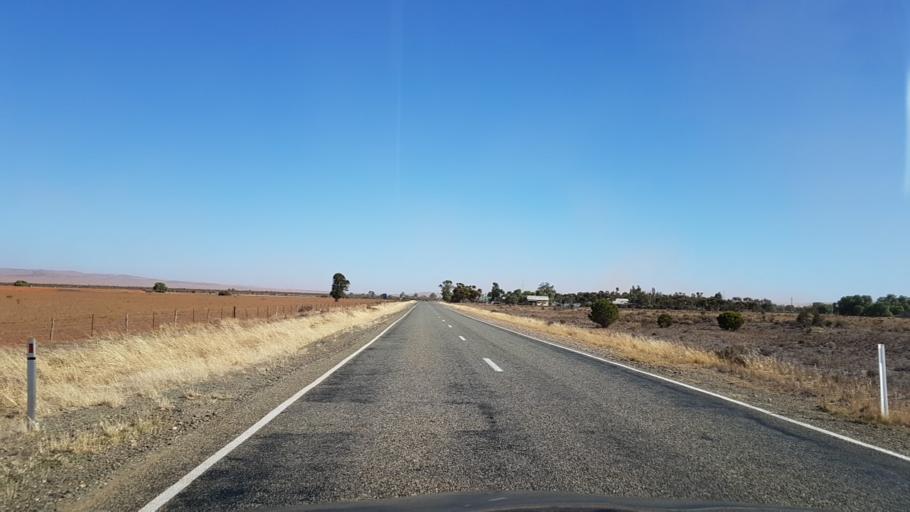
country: AU
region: South Australia
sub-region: Peterborough
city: Peterborough
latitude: -33.1489
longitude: 138.9255
